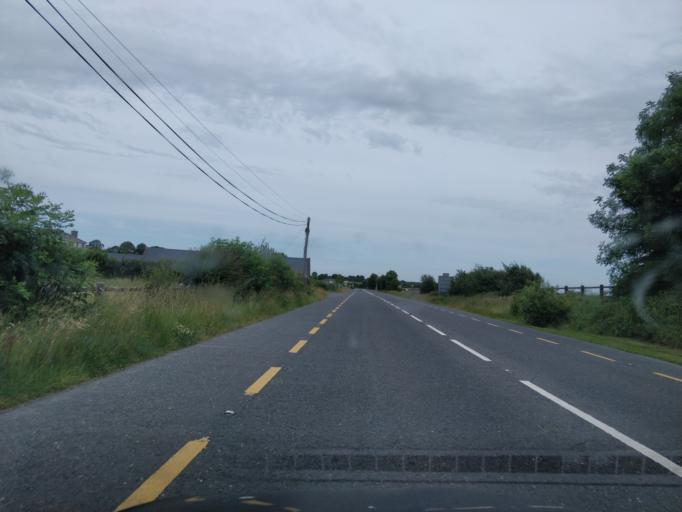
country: IE
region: Leinster
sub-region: Uibh Fhaili
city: Birr
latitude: 53.1491
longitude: -7.8406
